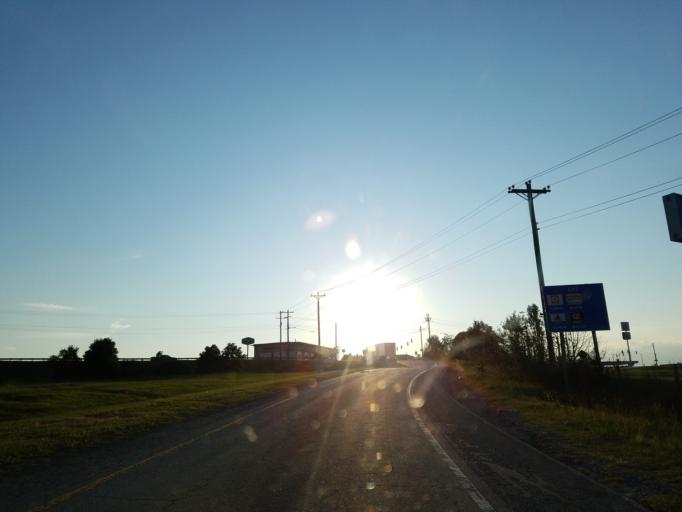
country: US
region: South Carolina
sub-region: Cherokee County
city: Gaffney
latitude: 35.0837
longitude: -81.7050
